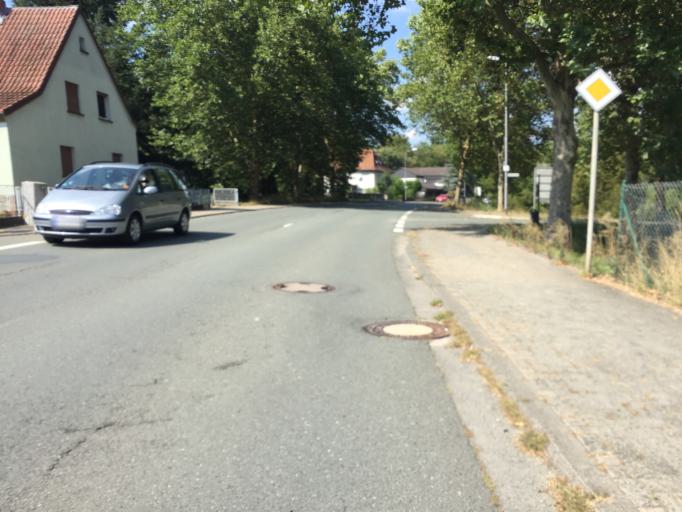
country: DE
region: Hesse
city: Solms
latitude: 50.5314
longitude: 8.4087
